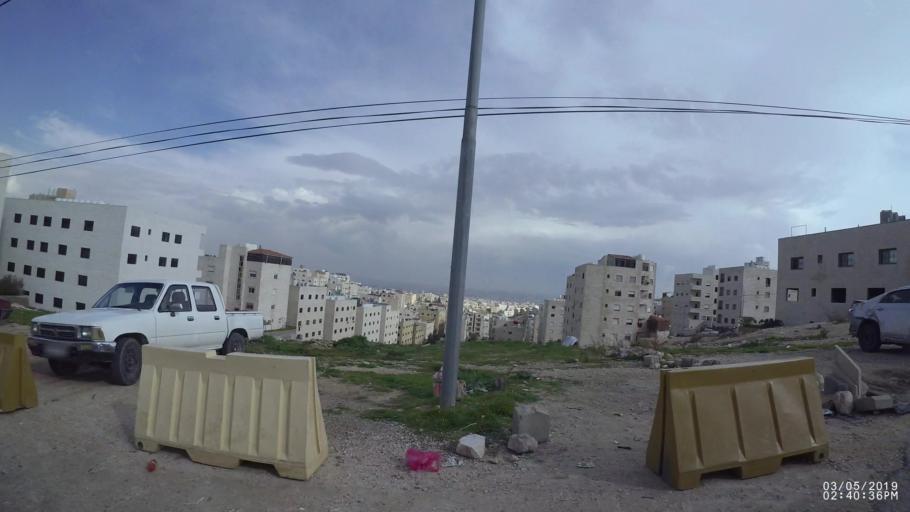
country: JO
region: Amman
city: Amman
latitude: 32.0128
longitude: 35.9376
